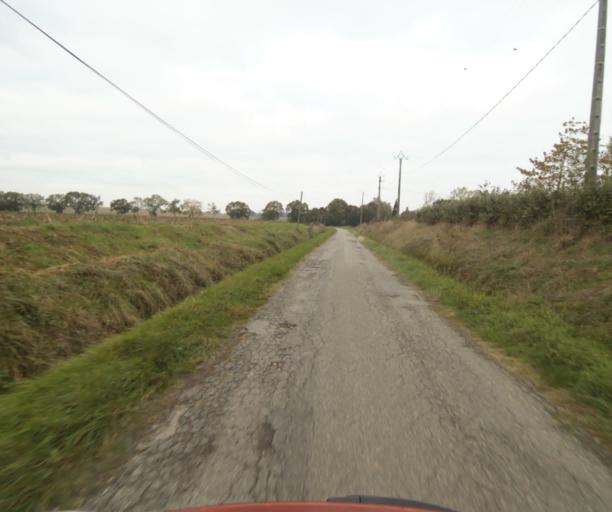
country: FR
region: Midi-Pyrenees
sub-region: Departement du Tarn-et-Garonne
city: Verdun-sur-Garonne
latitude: 43.8072
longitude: 1.2134
